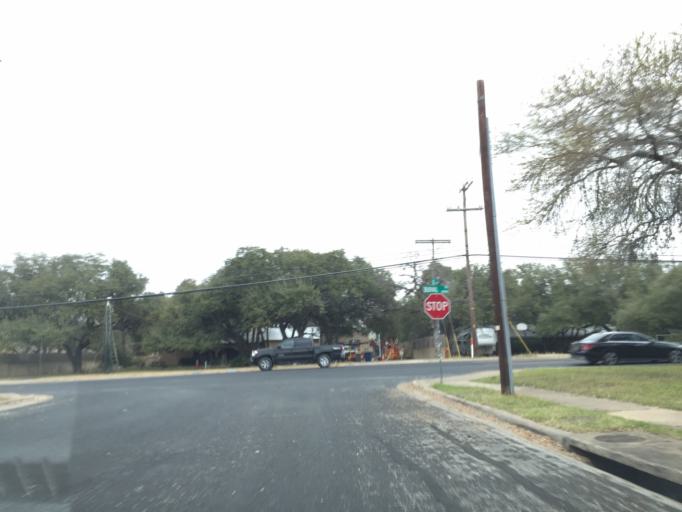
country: US
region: Texas
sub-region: Williamson County
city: Jollyville
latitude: 30.4149
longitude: -97.7374
